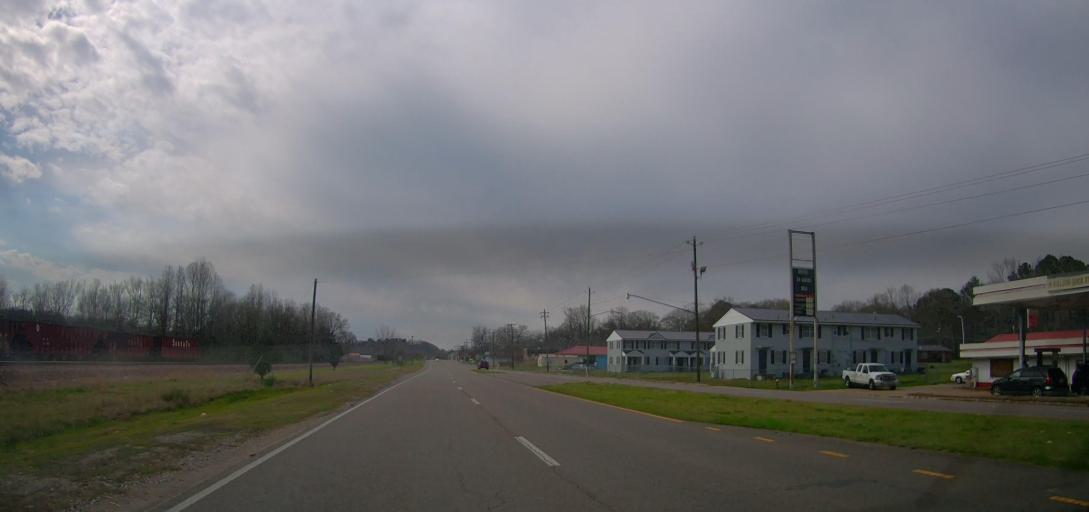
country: US
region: Alabama
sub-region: Walker County
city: Carbon Hill
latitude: 33.8862
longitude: -87.5227
